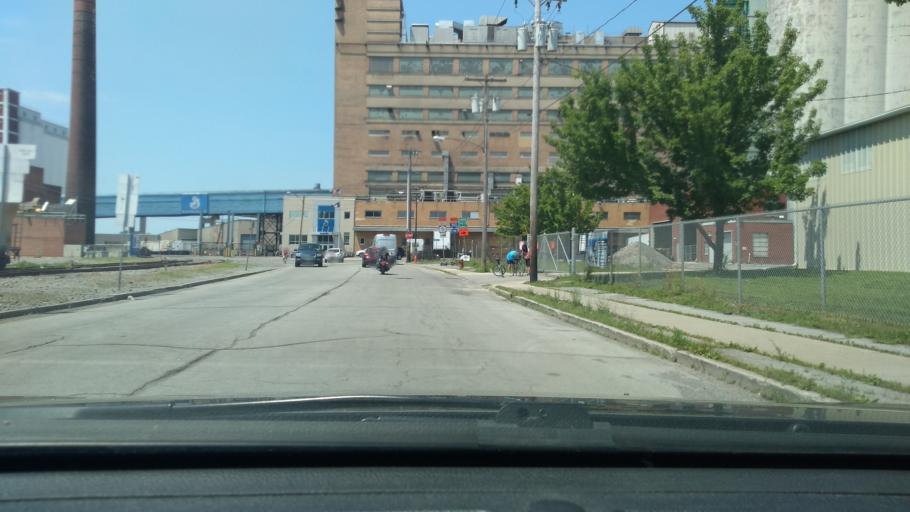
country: US
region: New York
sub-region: Erie County
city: Buffalo
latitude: 42.8702
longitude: -78.8741
